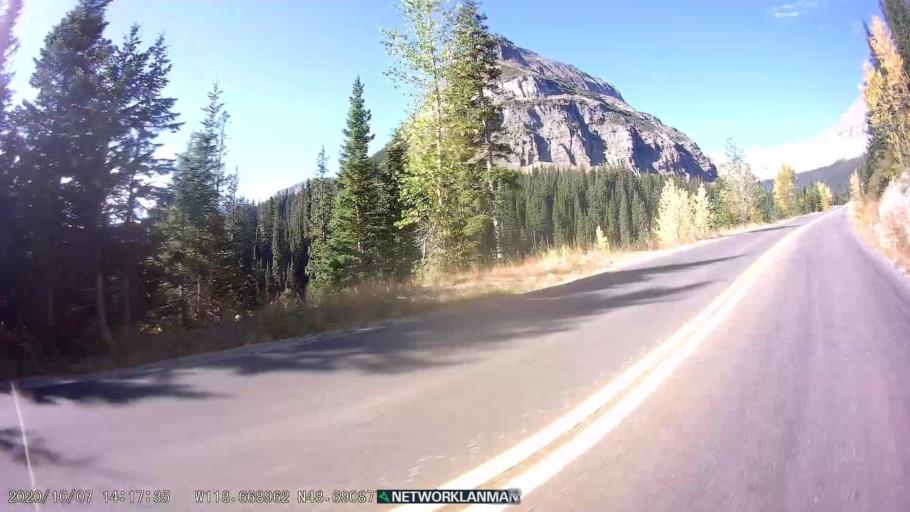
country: US
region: Montana
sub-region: Flathead County
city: Columbia Falls
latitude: 48.6922
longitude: -113.6680
